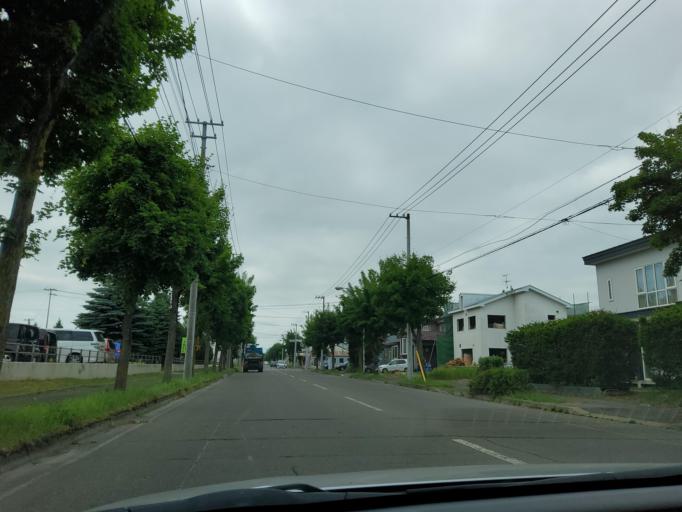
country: JP
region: Hokkaido
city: Obihiro
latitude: 42.9133
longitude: 143.1533
